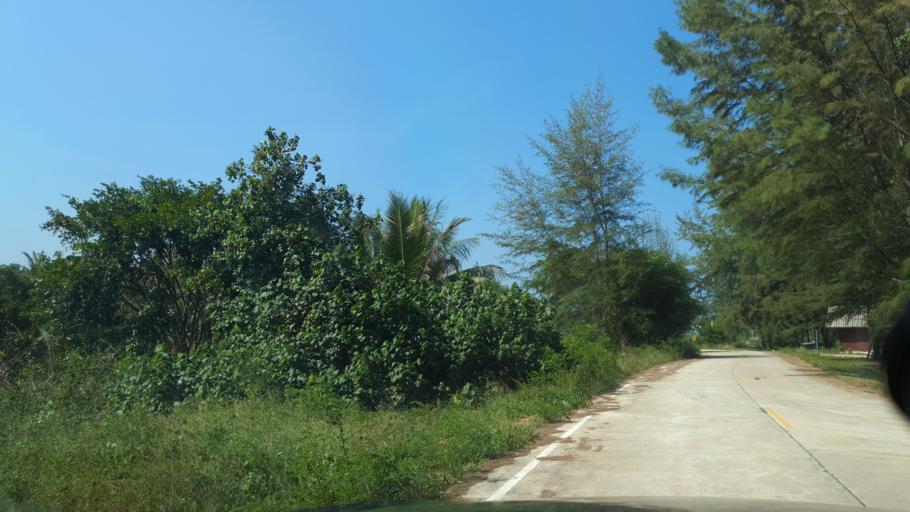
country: TH
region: Surat Thani
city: Tha Chana
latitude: 9.5989
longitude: 99.2094
